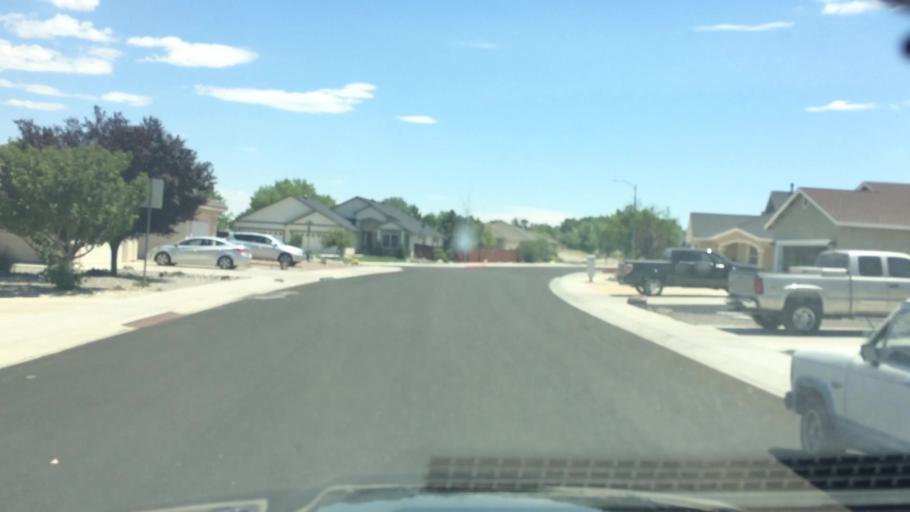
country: US
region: Nevada
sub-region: Lyon County
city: Fernley
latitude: 39.5837
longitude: -119.1422
